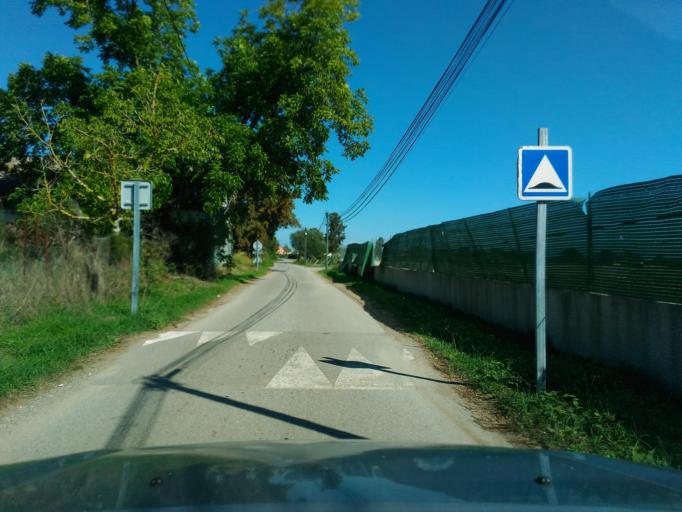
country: FR
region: Corsica
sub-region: Departement de la Haute-Corse
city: Aleria
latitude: 42.1082
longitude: 9.4775
